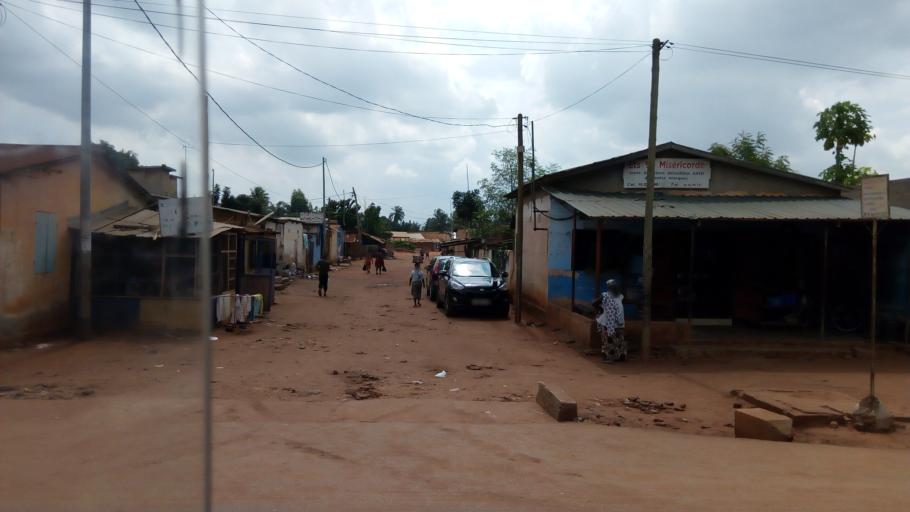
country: TG
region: Maritime
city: Tsevie
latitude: 6.4288
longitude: 1.2129
